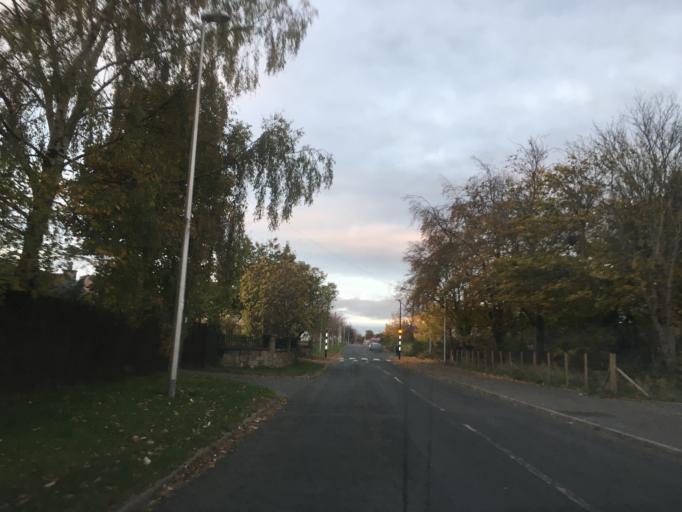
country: GB
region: Scotland
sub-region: Midlothian
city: Loanhead
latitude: 55.8708
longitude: -3.1849
